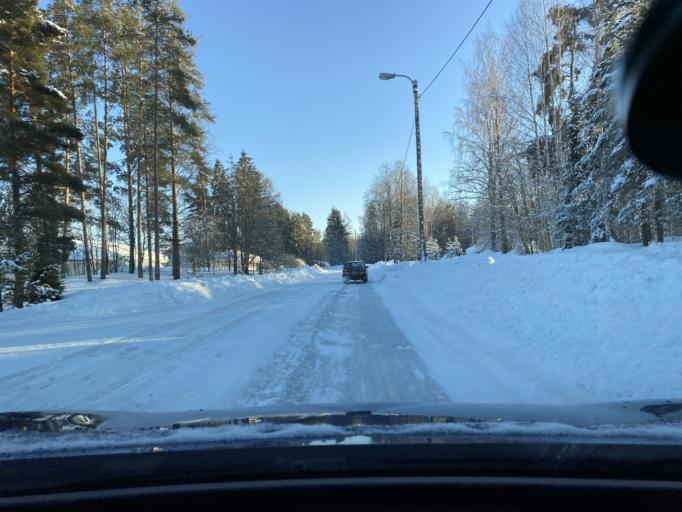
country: FI
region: Southern Savonia
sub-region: Mikkeli
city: Kangasniemi
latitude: 61.9980
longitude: 26.6292
